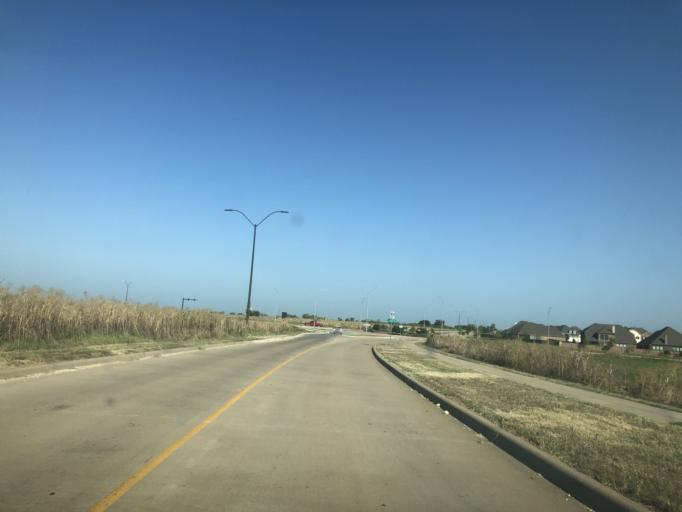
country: US
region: Texas
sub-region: Tarrant County
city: Crowley
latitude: 32.6066
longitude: -97.4178
